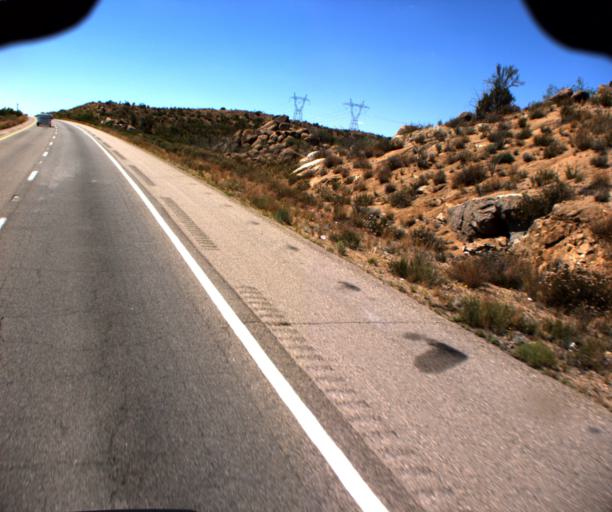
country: US
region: Arizona
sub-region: Yavapai County
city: Bagdad
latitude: 34.4722
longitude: -113.3184
